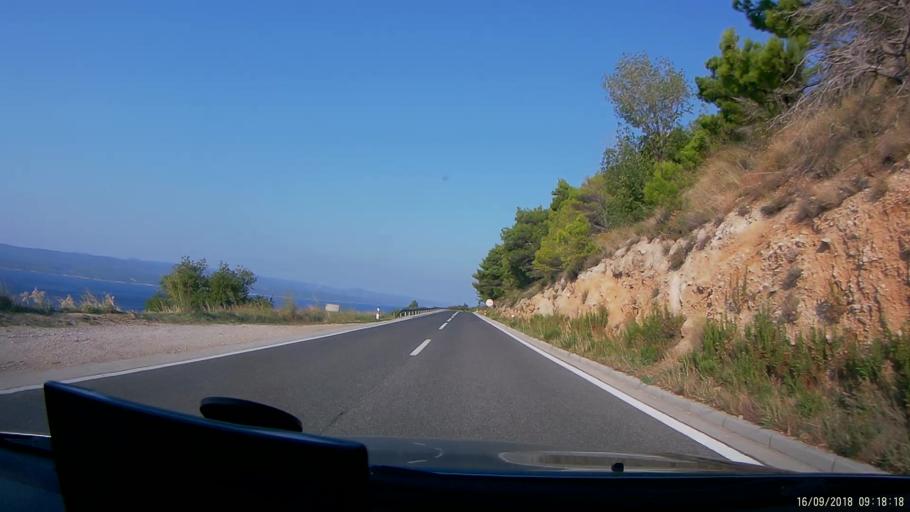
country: HR
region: Splitsko-Dalmatinska
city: Donja Brela
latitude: 43.4037
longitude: 16.8446
